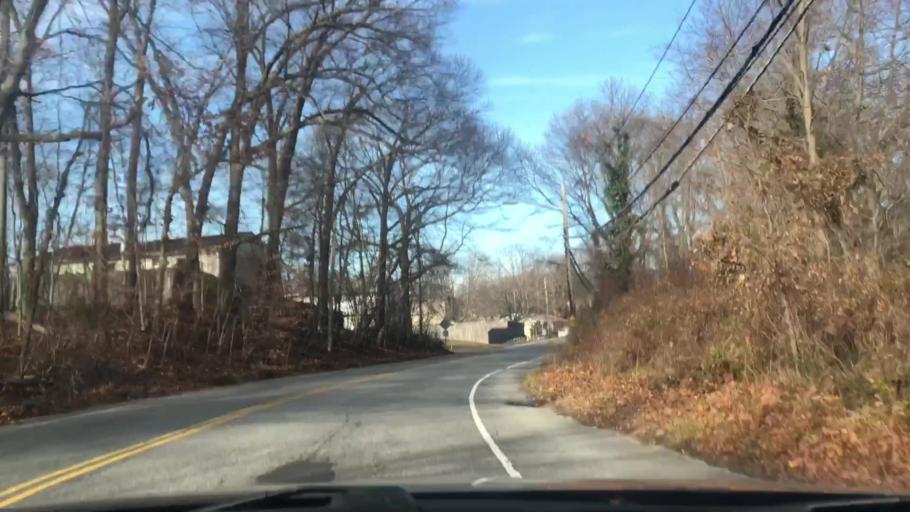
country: US
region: New York
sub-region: Suffolk County
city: Ronkonkoma
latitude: 40.8290
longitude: -73.1105
